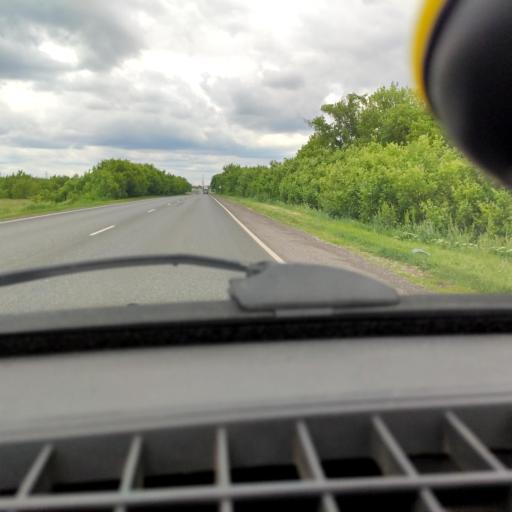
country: RU
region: Samara
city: Povolzhskiy
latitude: 53.6490
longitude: 49.6808
